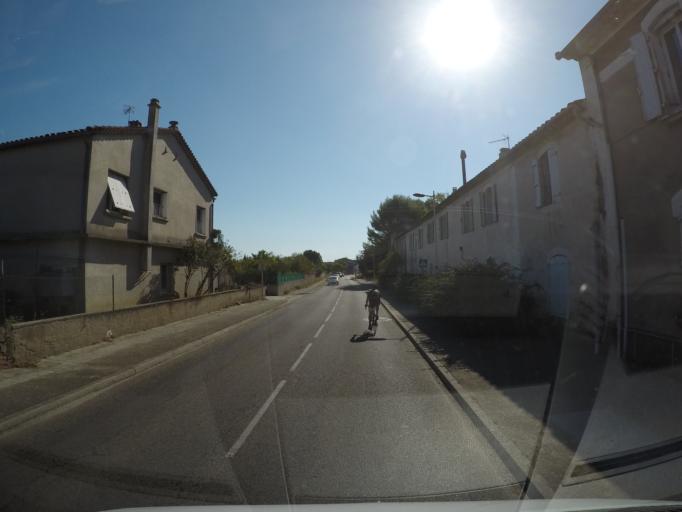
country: FR
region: Languedoc-Roussillon
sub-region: Departement du Gard
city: Boisset-et-Gaujac
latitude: 44.0278
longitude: 4.0190
